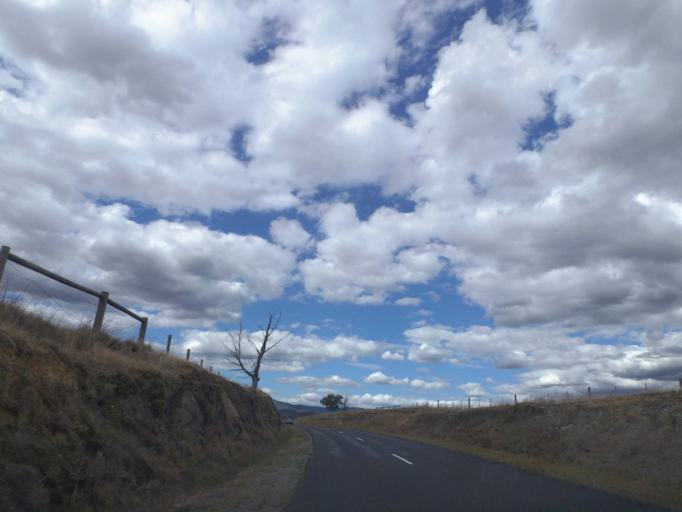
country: AU
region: Victoria
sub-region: Yarra Ranges
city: Yarra Glen
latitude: -37.6435
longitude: 145.4188
